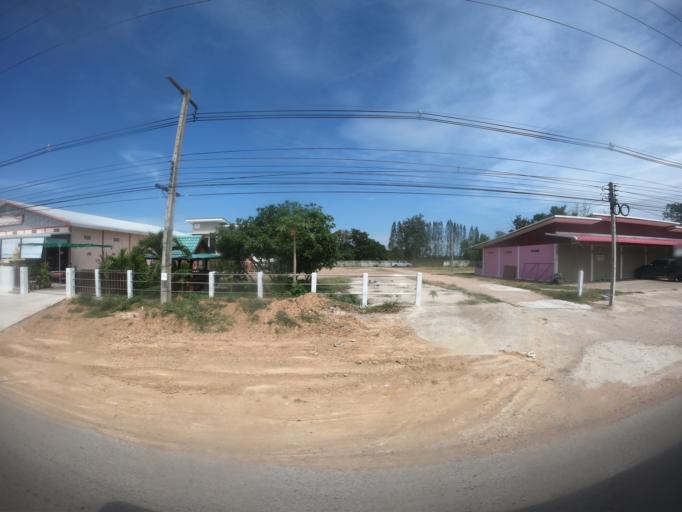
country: TH
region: Maha Sarakham
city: Chiang Yuen
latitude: 16.4443
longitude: 103.0090
